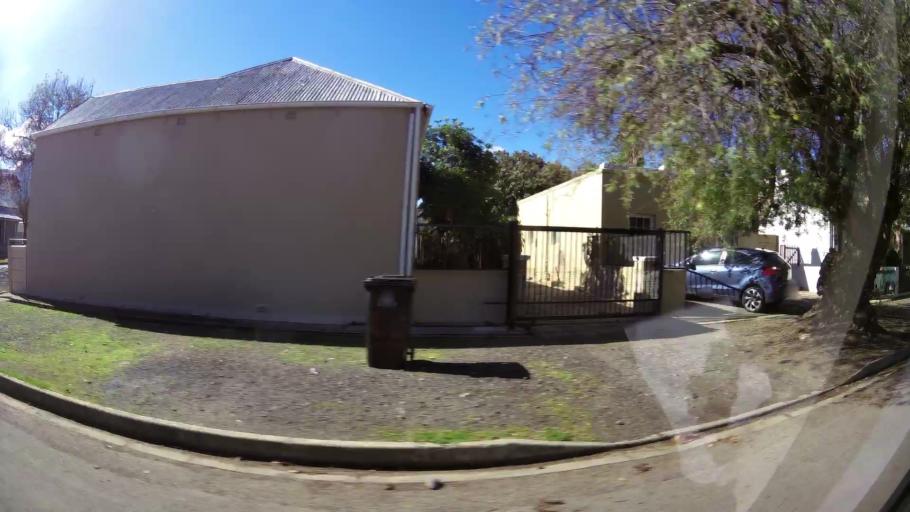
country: ZA
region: Western Cape
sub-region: Cape Winelands District Municipality
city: Ashton
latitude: -33.7989
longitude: 19.8864
